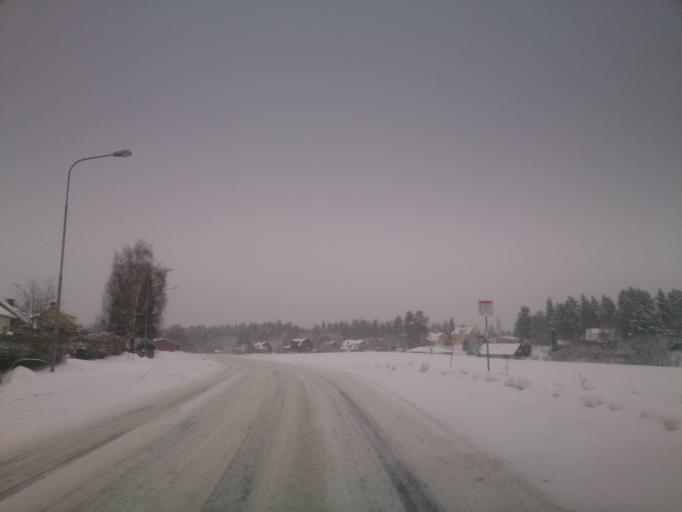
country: SE
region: OEstergoetland
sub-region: Finspangs Kommun
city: Finspang
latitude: 58.6837
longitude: 15.7515
